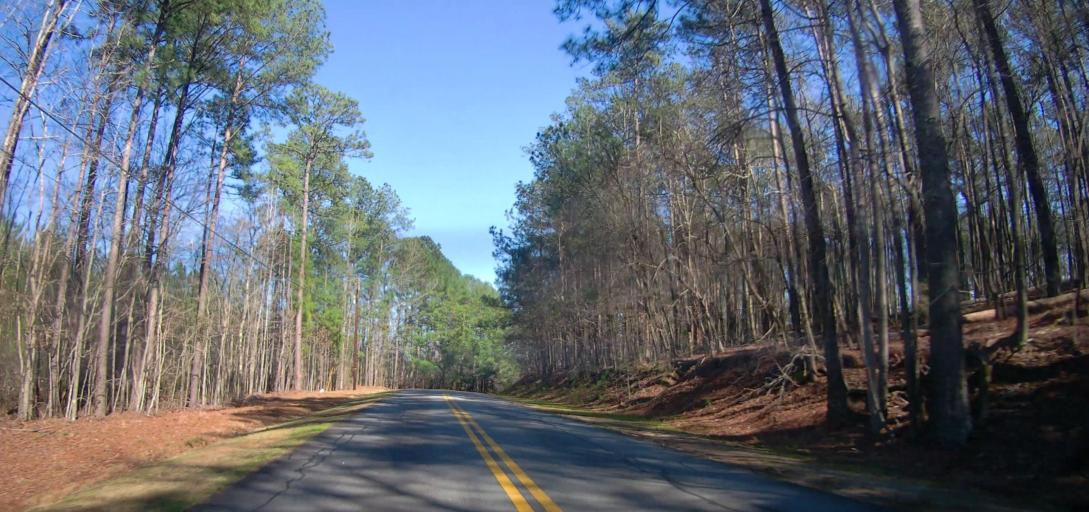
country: US
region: Georgia
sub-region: Butts County
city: Indian Springs
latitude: 33.2537
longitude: -83.9329
